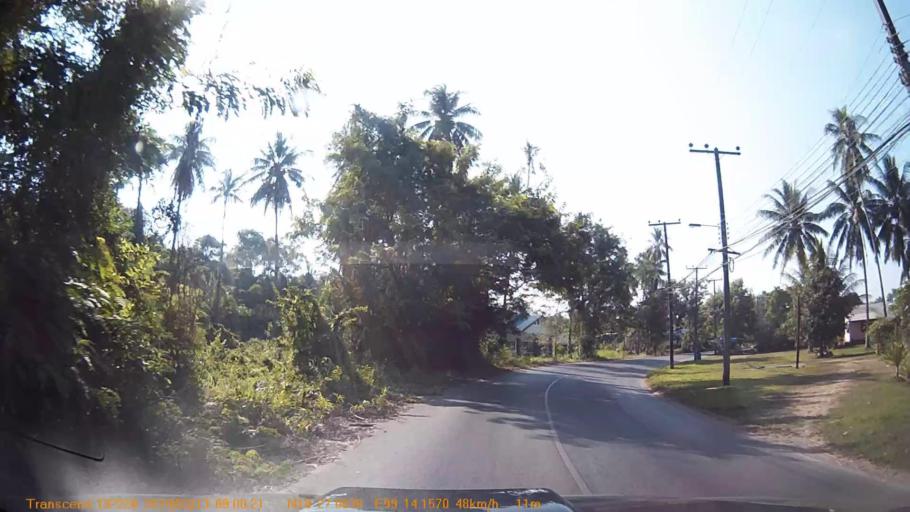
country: TH
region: Chumphon
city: Chumphon
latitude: 10.4499
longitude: 99.2361
